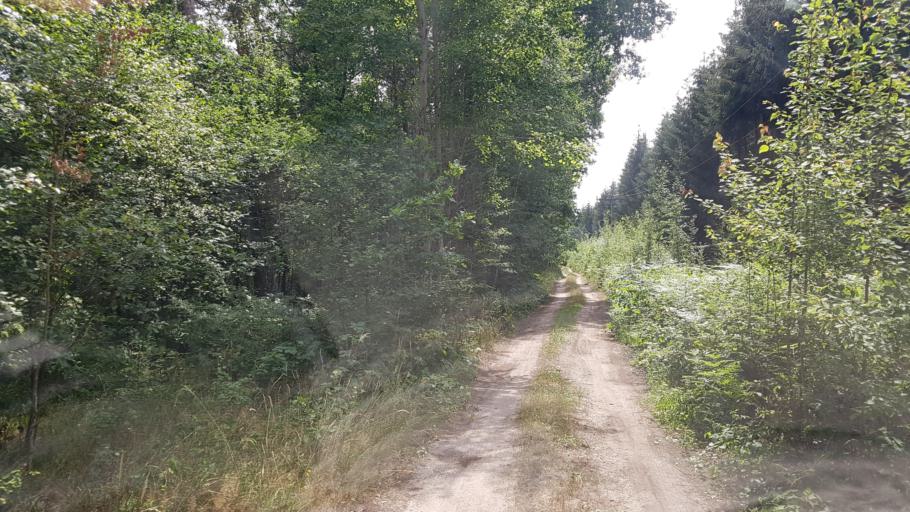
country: DE
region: Brandenburg
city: Sallgast
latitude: 51.5953
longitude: 13.9023
